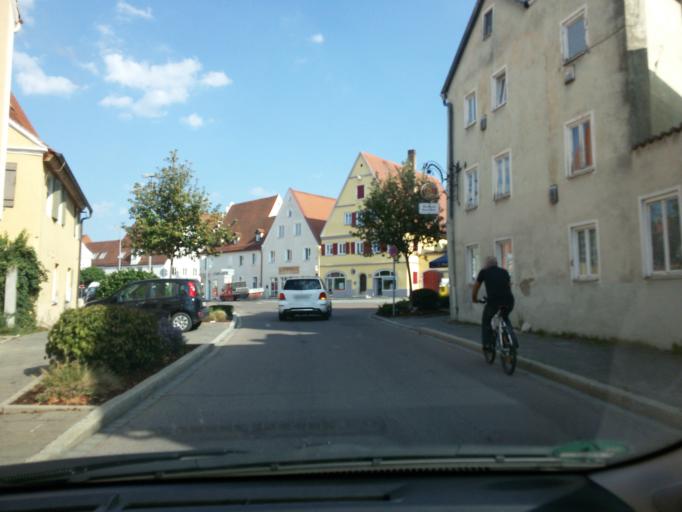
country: DE
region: Bavaria
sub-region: Swabia
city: Noerdlingen
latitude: 48.8491
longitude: 10.4890
